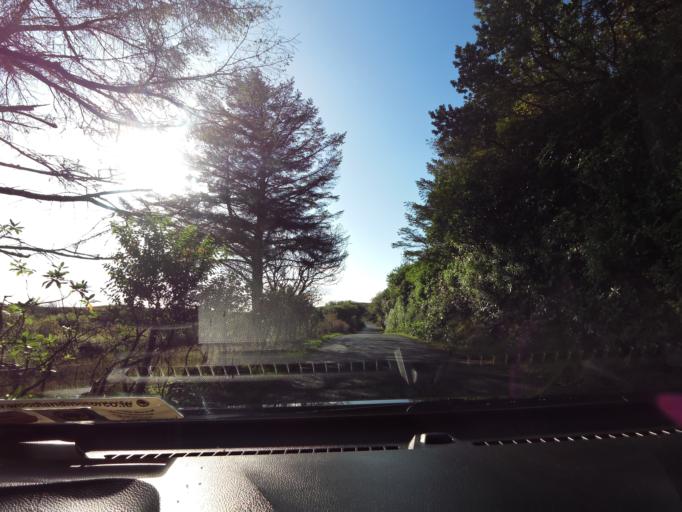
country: IE
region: Connaught
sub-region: Maigh Eo
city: Westport
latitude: 53.8983
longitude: -9.7935
